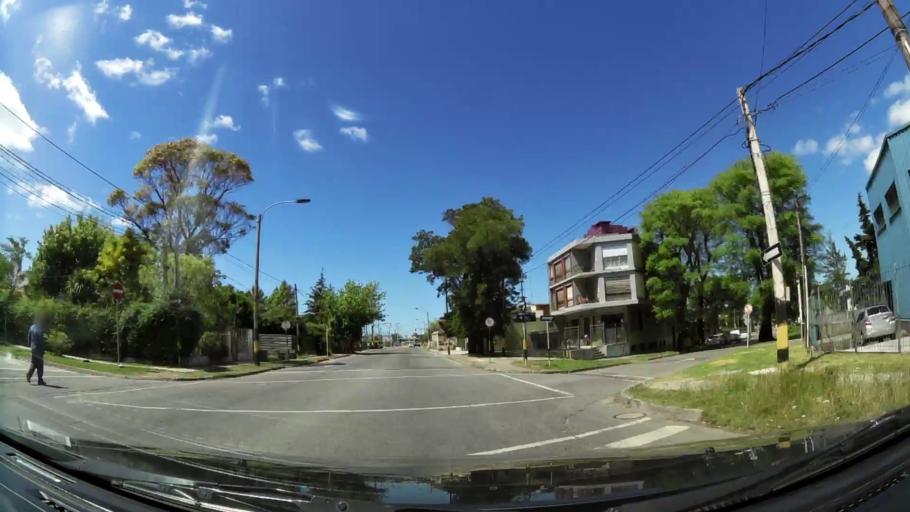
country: UY
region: Montevideo
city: Montevideo
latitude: -34.8524
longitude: -56.1328
